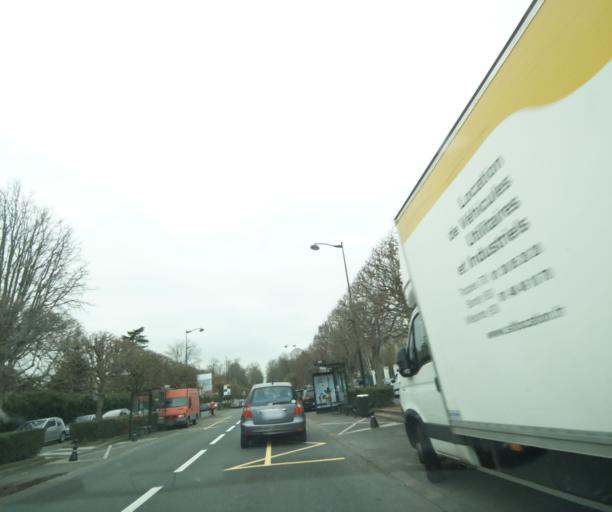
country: FR
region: Ile-de-France
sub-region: Departement des Yvelines
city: Saint-Germain-en-Laye
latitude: 48.9037
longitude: 2.0839
